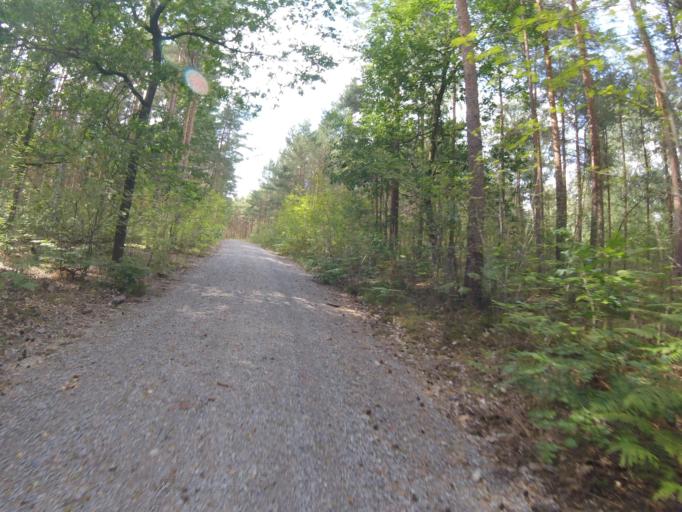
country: DE
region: Brandenburg
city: Halbe
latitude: 52.0604
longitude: 13.7910
